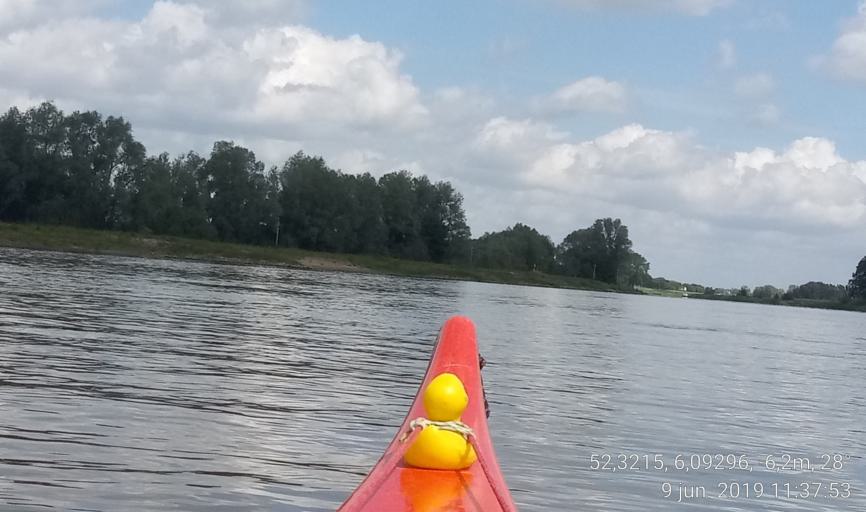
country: NL
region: Overijssel
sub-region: Gemeente Olst-Wijhe
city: Olst
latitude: 52.3215
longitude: 6.0930
